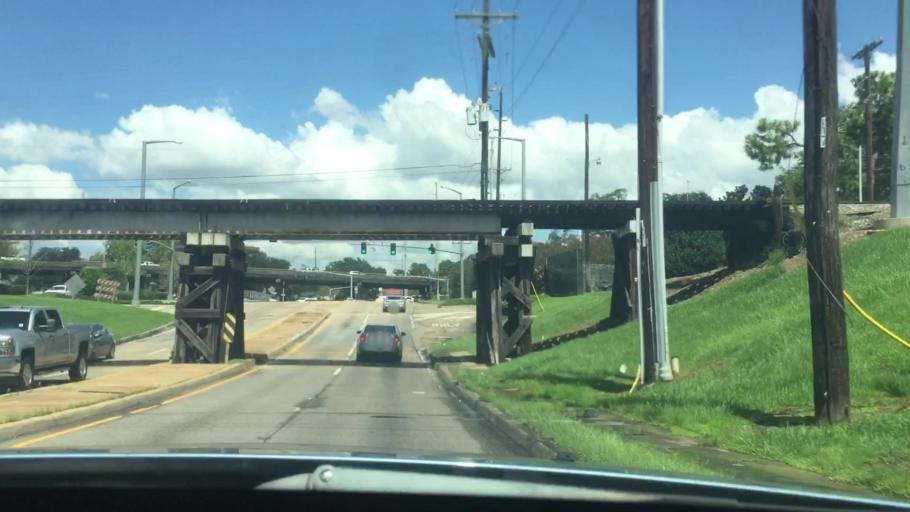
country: US
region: Louisiana
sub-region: East Baton Rouge Parish
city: Baton Rouge
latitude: 30.4219
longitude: -91.1523
